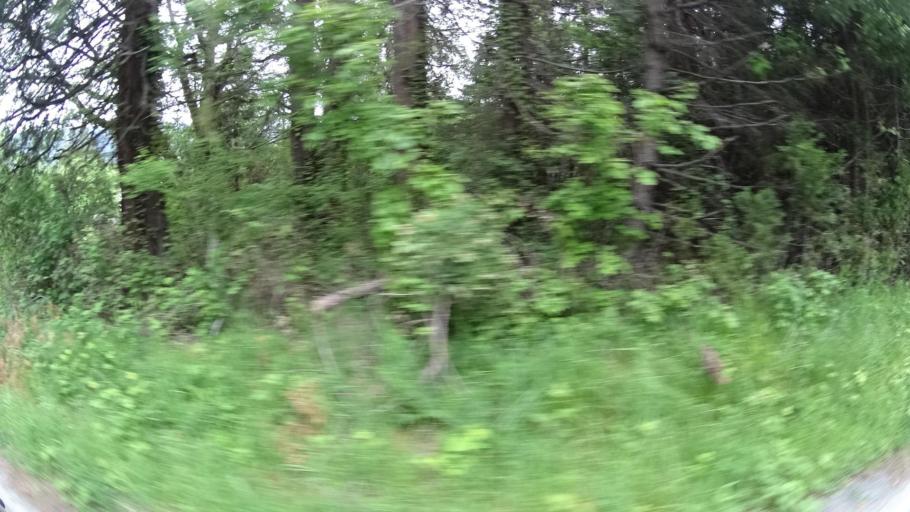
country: US
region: California
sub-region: Humboldt County
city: Willow Creek
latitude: 41.0852
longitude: -123.7060
